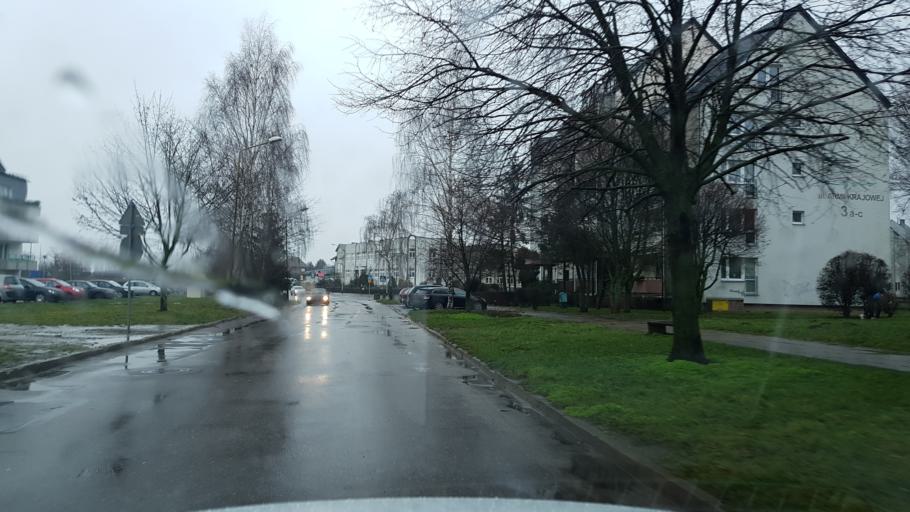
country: PL
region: West Pomeranian Voivodeship
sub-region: Powiat stargardzki
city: Stargard Szczecinski
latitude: 53.3152
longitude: 15.0343
